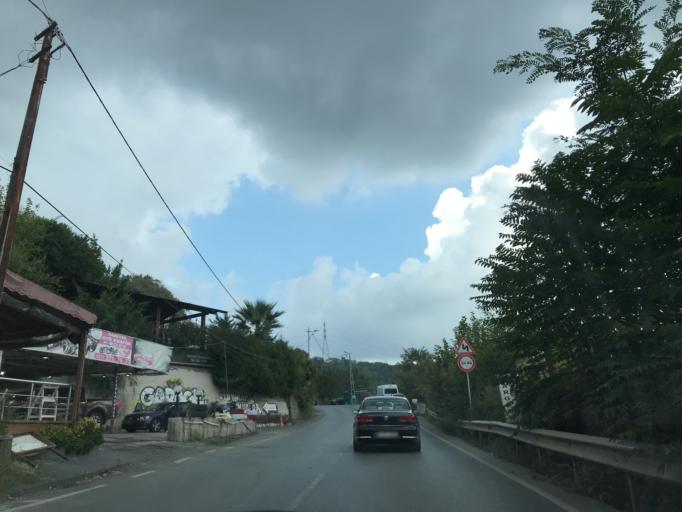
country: TR
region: Istanbul
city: Arikoey
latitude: 41.1796
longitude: 29.0467
